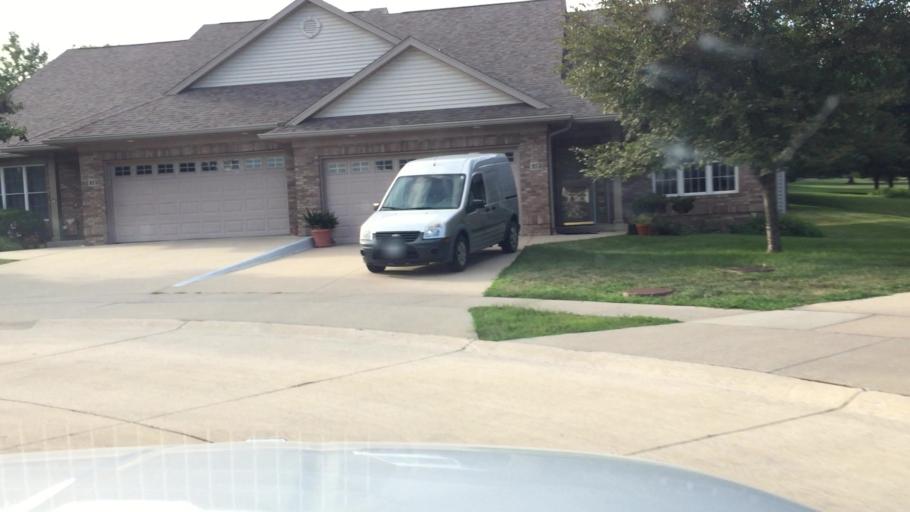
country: US
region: Iowa
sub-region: Johnson County
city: Iowa City
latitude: 41.6624
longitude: -91.4930
